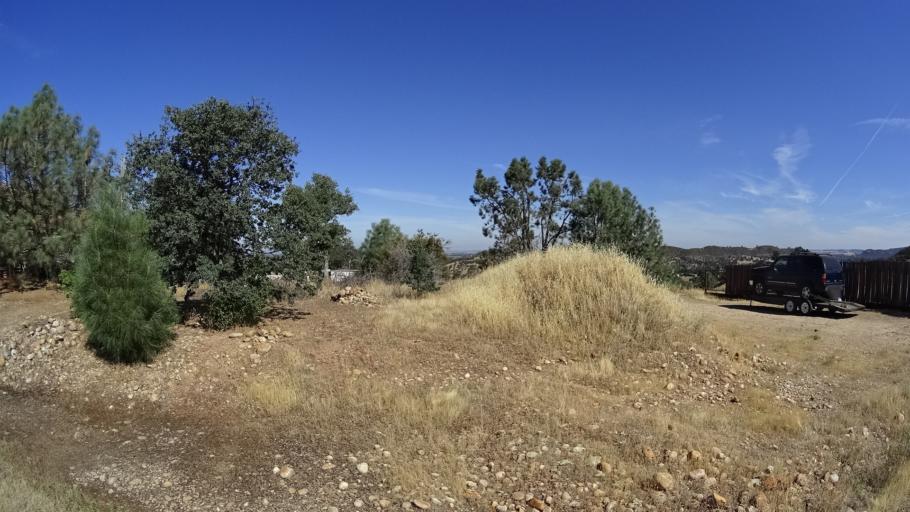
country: US
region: California
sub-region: Calaveras County
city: Valley Springs
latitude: 38.1722
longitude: -120.8644
